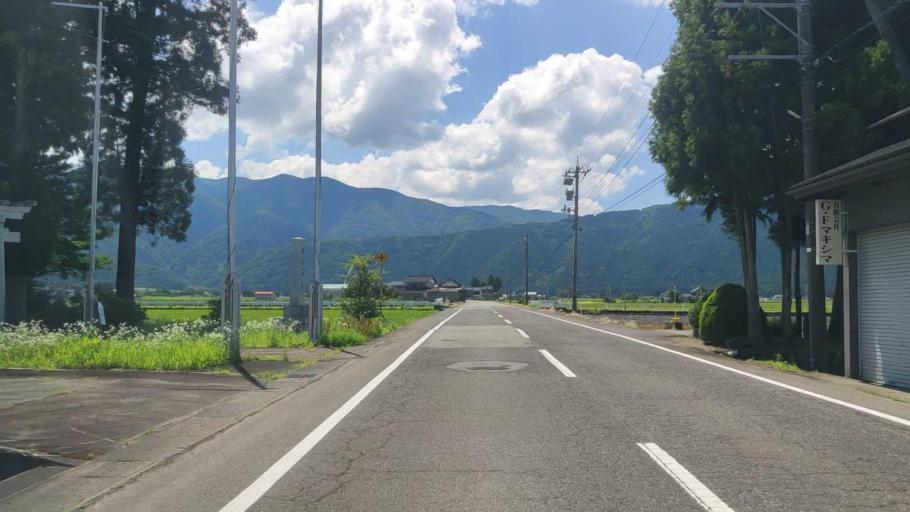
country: JP
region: Fukui
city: Ono
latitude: 35.9532
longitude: 136.5384
